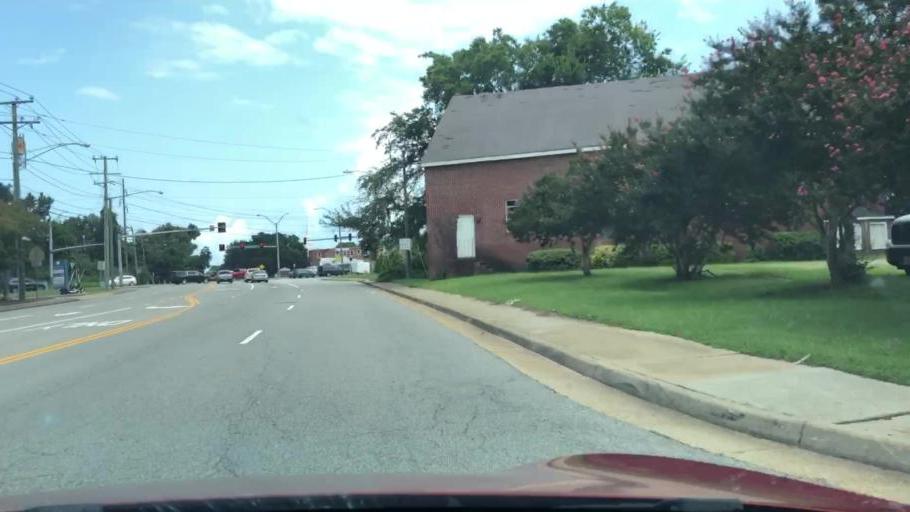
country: US
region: Virginia
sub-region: City of Norfolk
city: Norfolk
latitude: 36.8978
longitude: -76.1381
